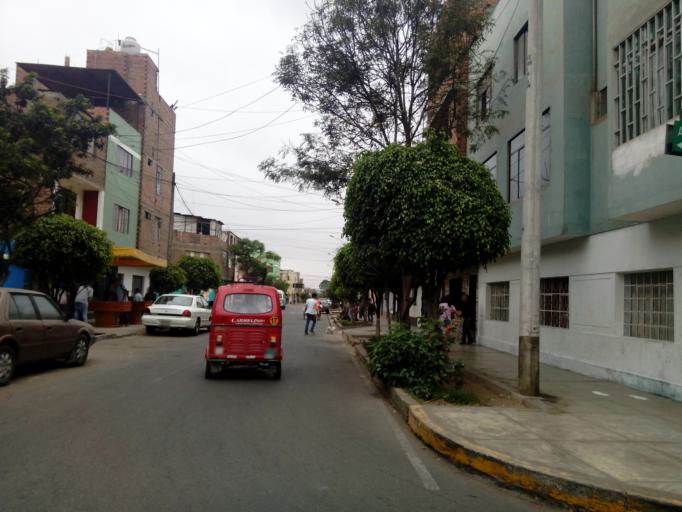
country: PE
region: Callao
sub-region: Callao
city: Callao
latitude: -12.0420
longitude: -77.0938
